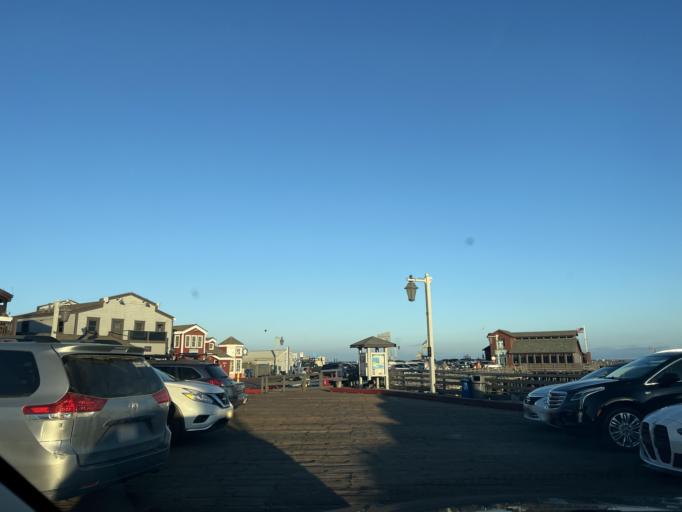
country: US
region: California
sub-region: Santa Barbara County
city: Santa Barbara
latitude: 34.4101
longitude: -119.6859
